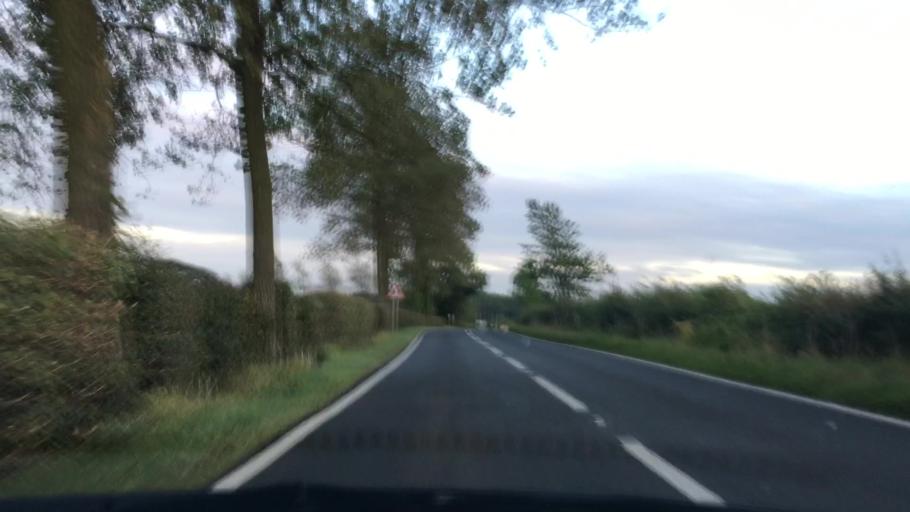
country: GB
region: England
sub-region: North East Lincolnshire
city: Wold Newton
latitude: 53.4586
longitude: -0.0909
